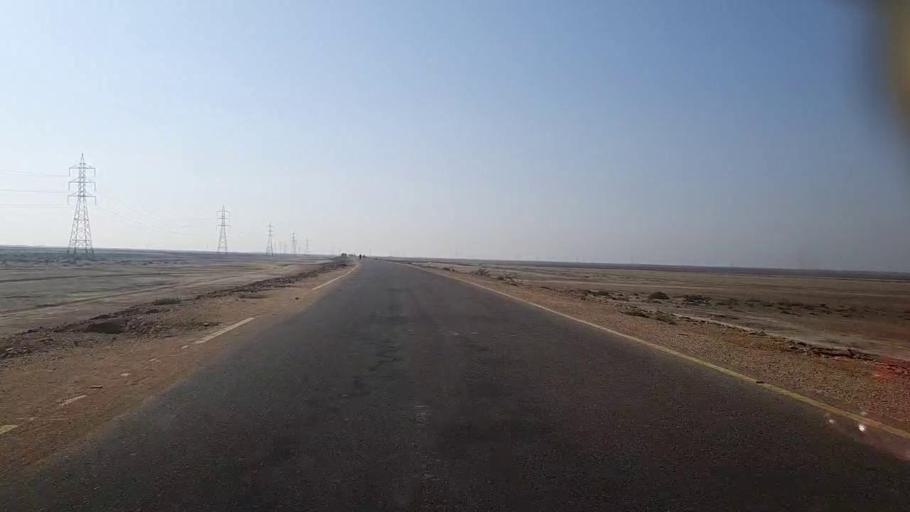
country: PK
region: Sindh
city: Mirpur Sakro
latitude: 24.6103
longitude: 67.4971
